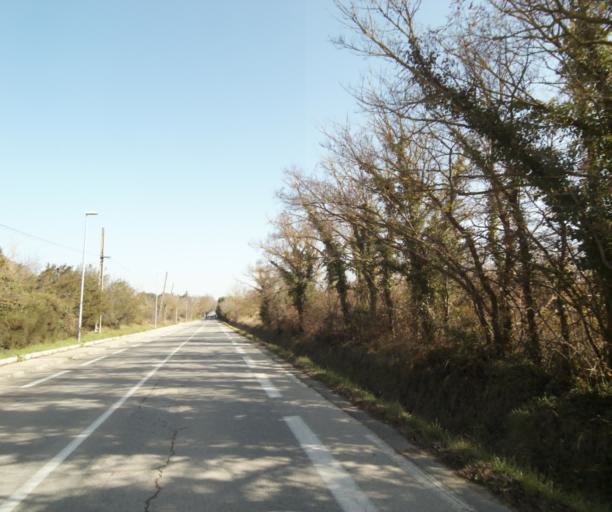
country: FR
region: Provence-Alpes-Cote d'Azur
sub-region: Departement des Bouches-du-Rhone
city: Aix-en-Provence
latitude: 43.5518
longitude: 5.4575
